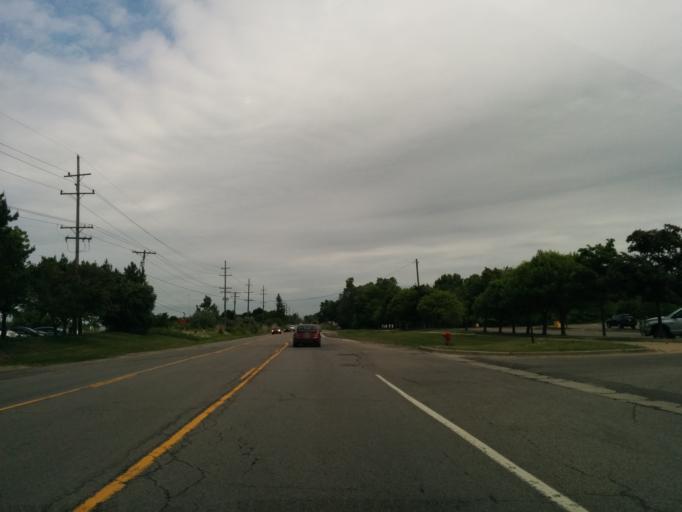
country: US
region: Michigan
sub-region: Oakland County
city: Walled Lake
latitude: 42.5283
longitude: -83.4375
